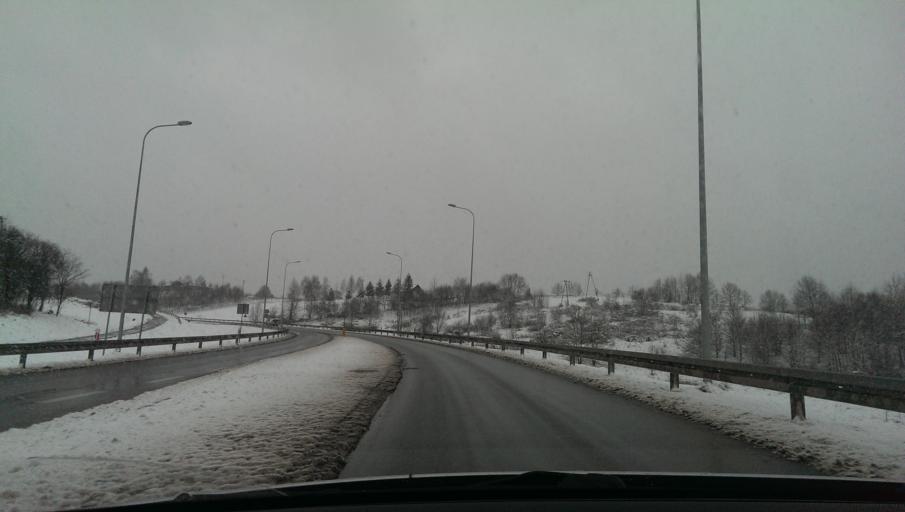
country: PL
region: Subcarpathian Voivodeship
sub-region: Powiat brzozowski
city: Brzozow
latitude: 49.6914
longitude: 22.0303
